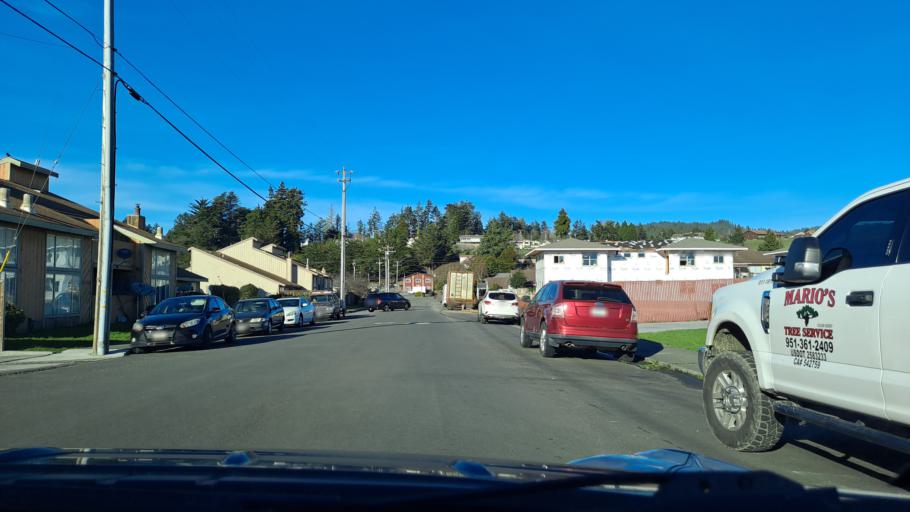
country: US
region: California
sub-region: Humboldt County
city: Fortuna
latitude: 40.5924
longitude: -124.1432
